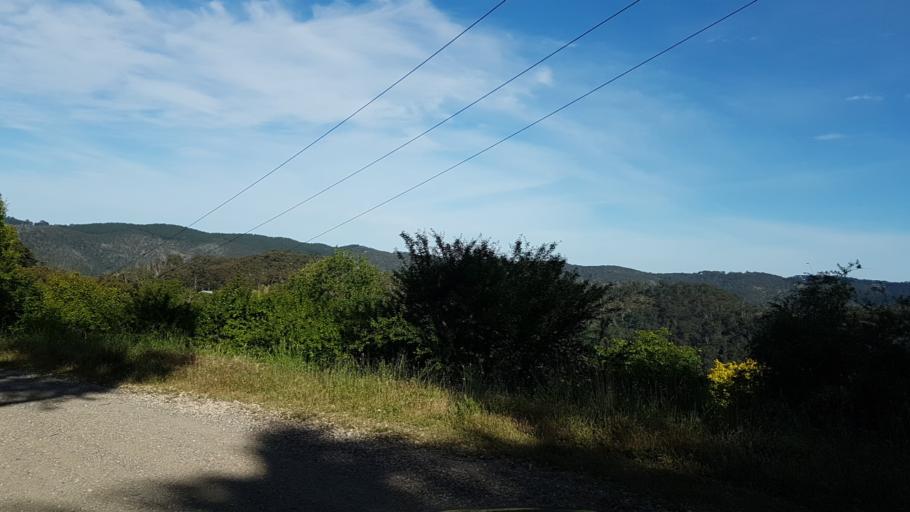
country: AU
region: South Australia
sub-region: Adelaide Hills
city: Adelaide Hills
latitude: -34.9125
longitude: 138.7600
